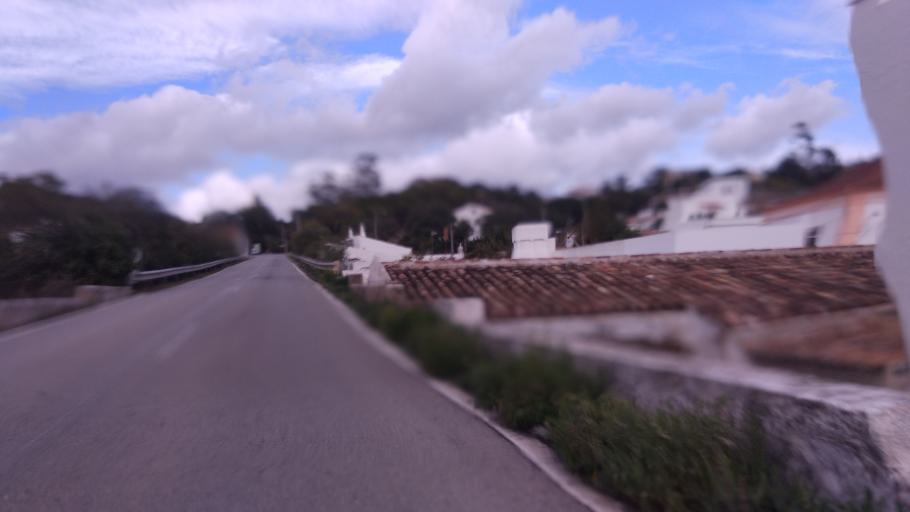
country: PT
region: Faro
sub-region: Sao Bras de Alportel
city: Sao Bras de Alportel
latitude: 37.1758
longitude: -7.9094
